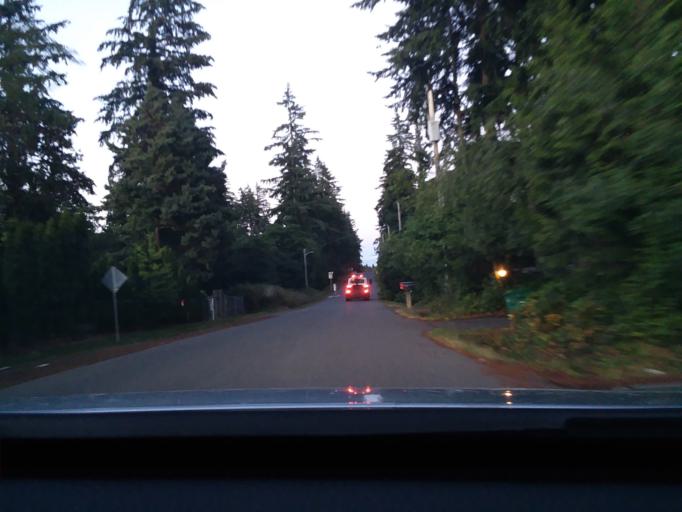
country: US
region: Washington
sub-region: King County
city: Shoreline
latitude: 47.7505
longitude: -122.3441
